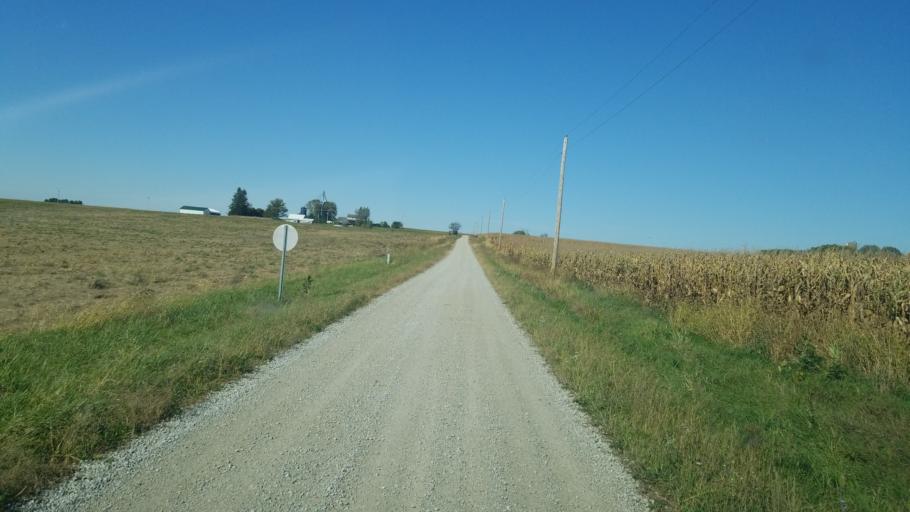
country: US
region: Ohio
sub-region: Huron County
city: New London
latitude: 41.0441
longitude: -82.3459
